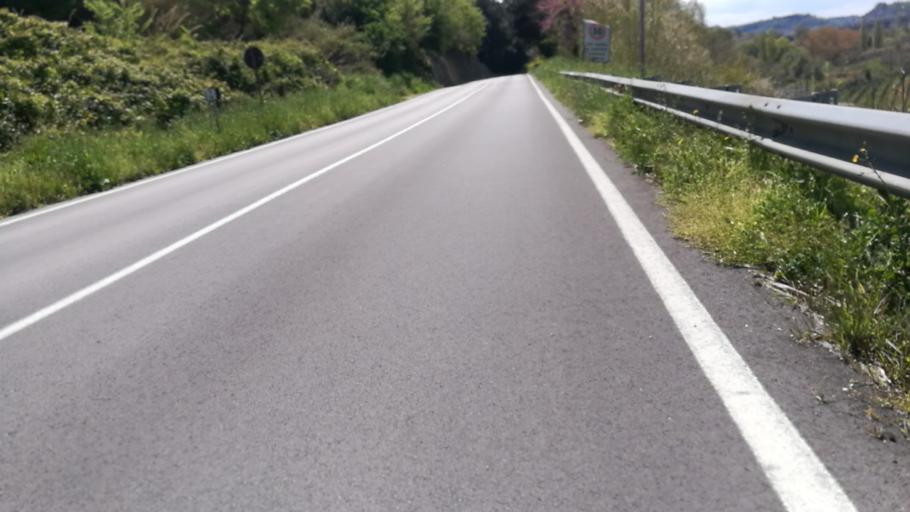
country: IT
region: Abruzzo
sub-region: Provincia di Chieti
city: Marina di San Vito
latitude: 42.3006
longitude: 14.4420
